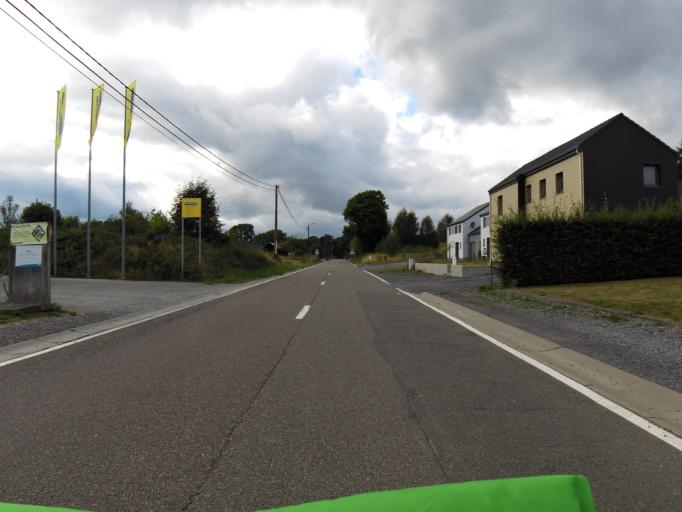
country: BE
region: Wallonia
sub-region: Province de Namur
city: Bievre
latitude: 49.9364
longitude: 5.0296
